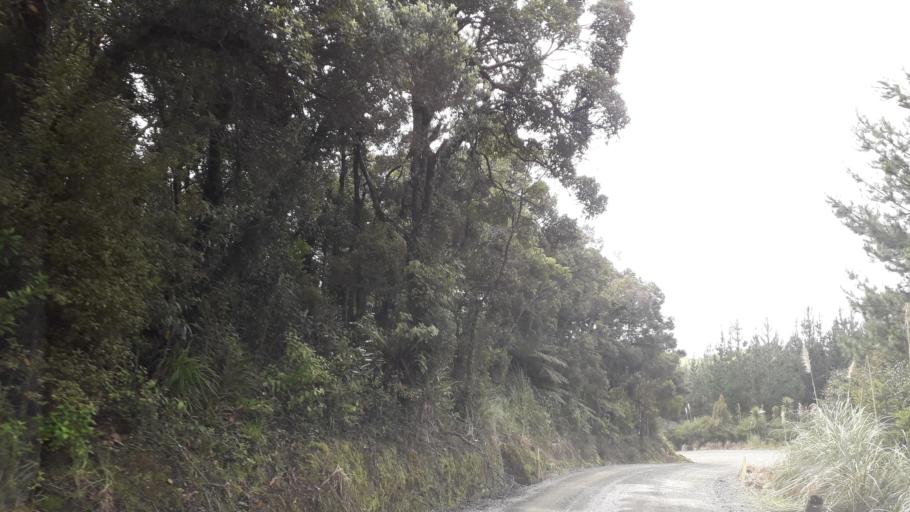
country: NZ
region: Northland
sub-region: Far North District
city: Kaitaia
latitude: -35.1962
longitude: 173.2847
